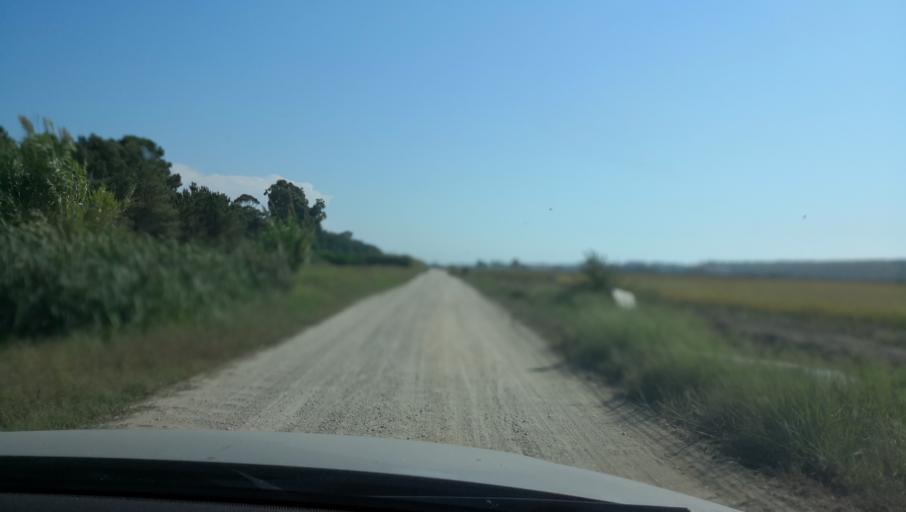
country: PT
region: Setubal
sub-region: Setubal
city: Setubal
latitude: 38.3890
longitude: -8.7897
